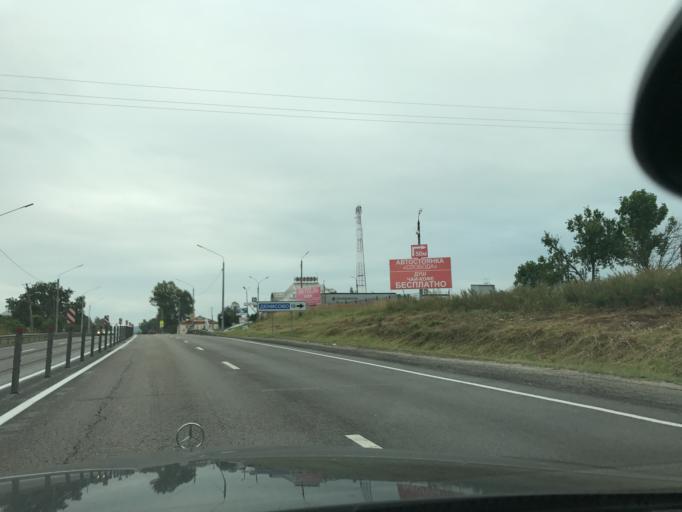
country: RU
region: Vladimir
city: Gorokhovets
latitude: 56.1696
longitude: 42.4396
